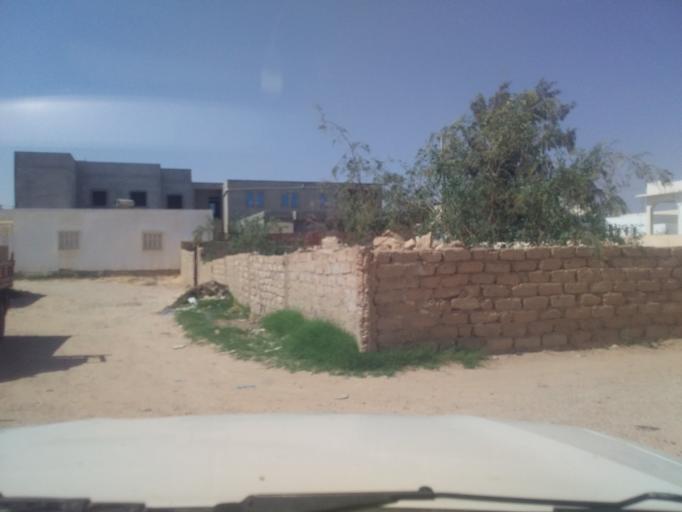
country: TN
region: Qabis
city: Matmata
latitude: 33.6168
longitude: 10.2909
